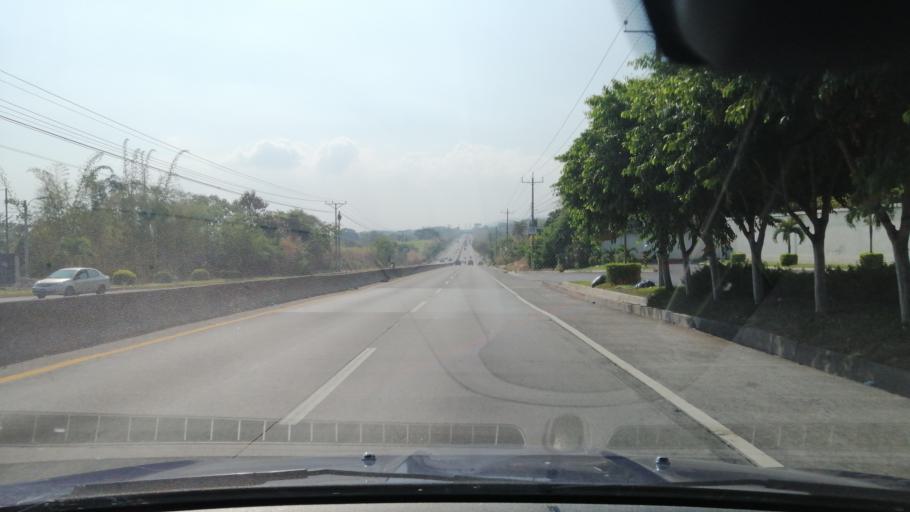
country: SV
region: San Salvador
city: Apopa
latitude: 13.7939
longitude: -89.2253
